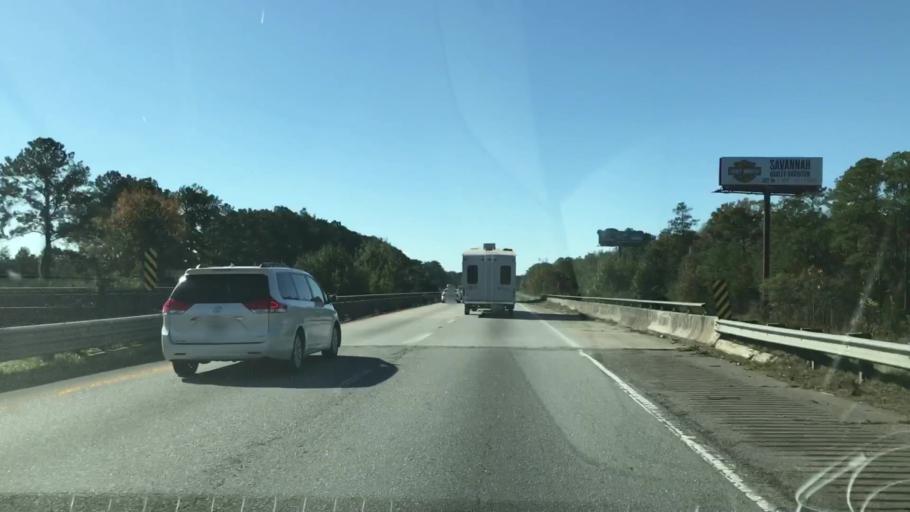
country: US
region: South Carolina
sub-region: Jasper County
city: Ridgeland
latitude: 32.5888
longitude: -80.9236
